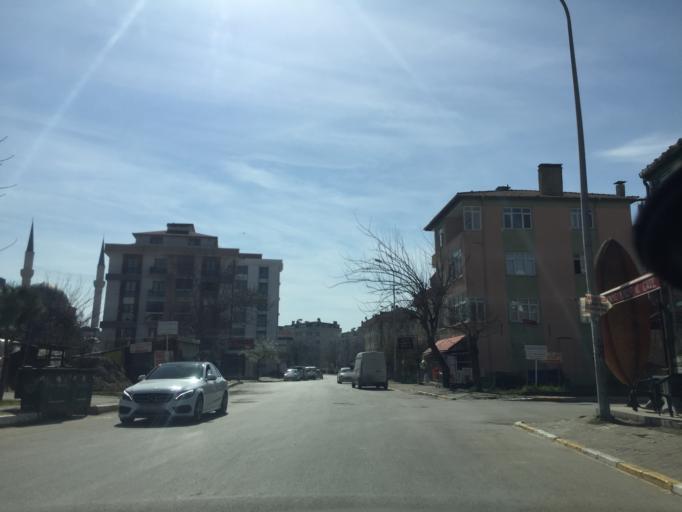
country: TR
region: Istanbul
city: Icmeler
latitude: 40.8292
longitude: 29.3185
